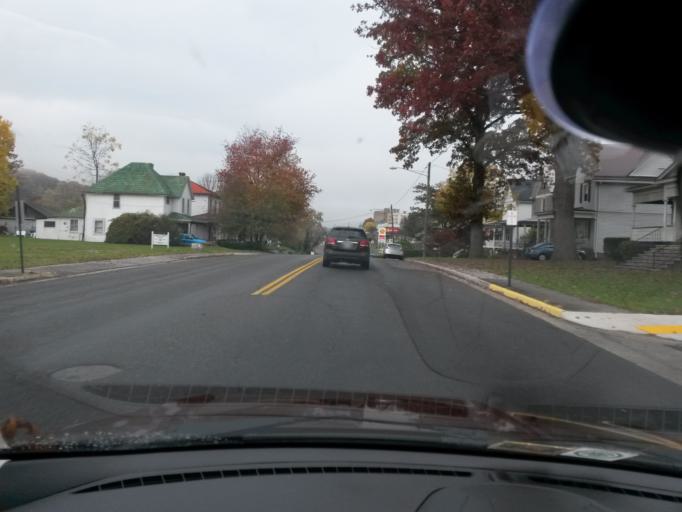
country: US
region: Virginia
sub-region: Alleghany County
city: Clifton Forge
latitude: 37.8121
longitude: -79.8361
